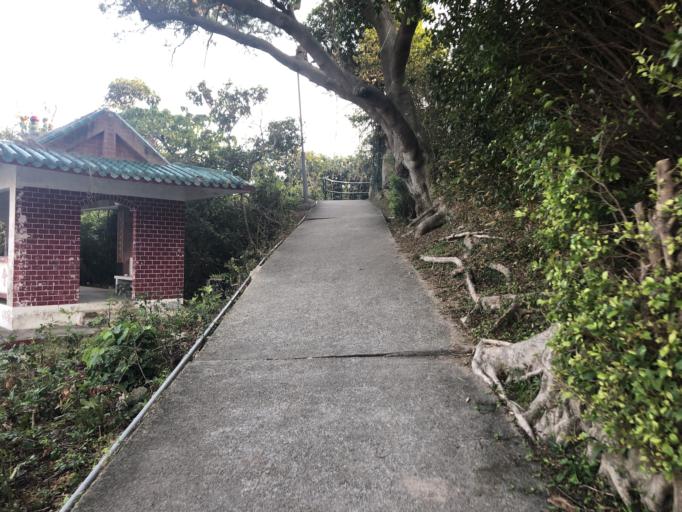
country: HK
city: Yung Shue Wan
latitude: 22.2012
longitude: 114.0196
